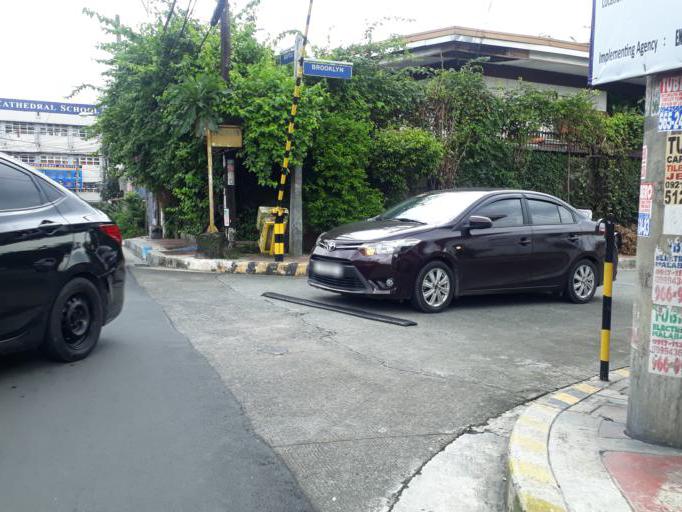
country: PH
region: Metro Manila
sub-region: San Juan
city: San Juan
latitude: 14.6206
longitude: 121.0435
